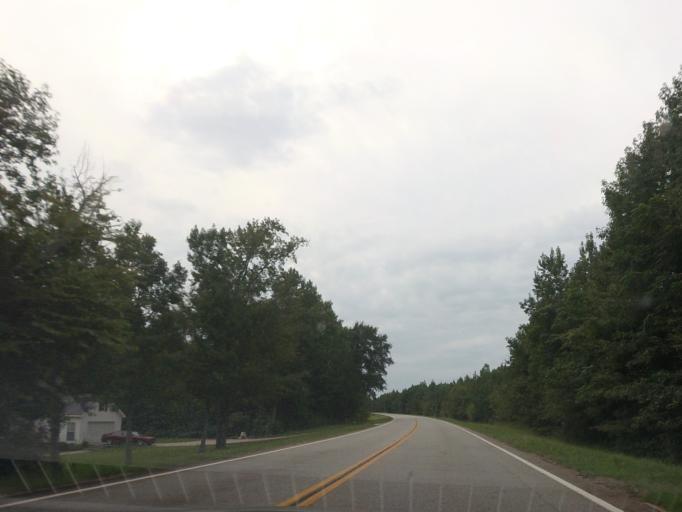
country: US
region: Georgia
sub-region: Twiggs County
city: Jeffersonville
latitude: 32.7088
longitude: -83.3818
